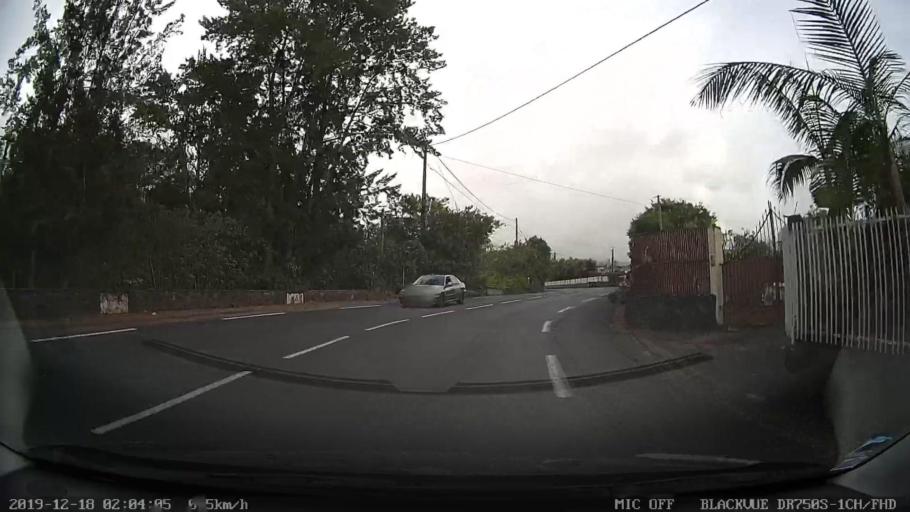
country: RE
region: Reunion
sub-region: Reunion
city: Le Tampon
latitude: -21.2454
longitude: 55.5243
